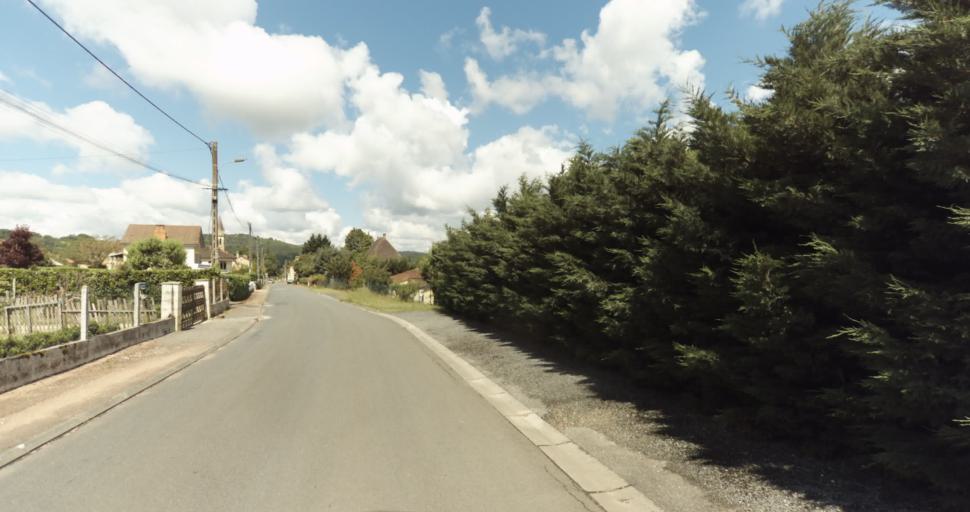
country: FR
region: Aquitaine
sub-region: Departement de la Dordogne
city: Le Bugue
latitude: 44.8429
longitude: 0.9122
